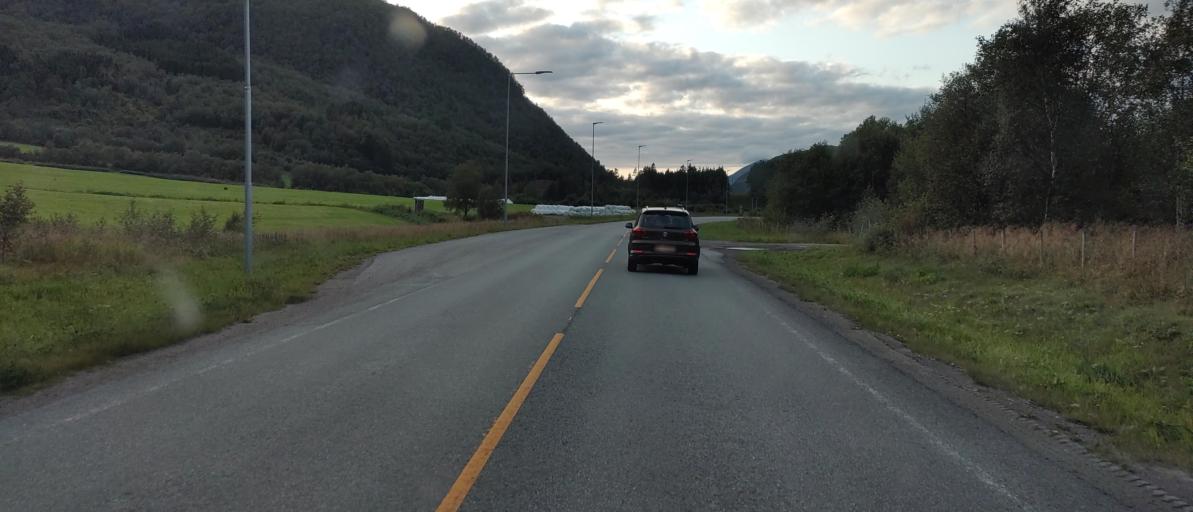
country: NO
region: More og Romsdal
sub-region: Molde
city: Molde
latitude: 62.7893
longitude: 7.2351
